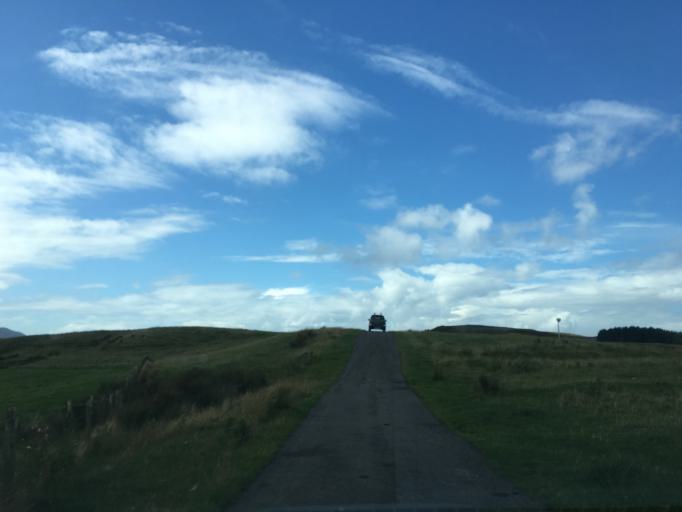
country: GB
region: Scotland
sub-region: Argyll and Bute
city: Oban
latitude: 56.2206
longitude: -5.6429
